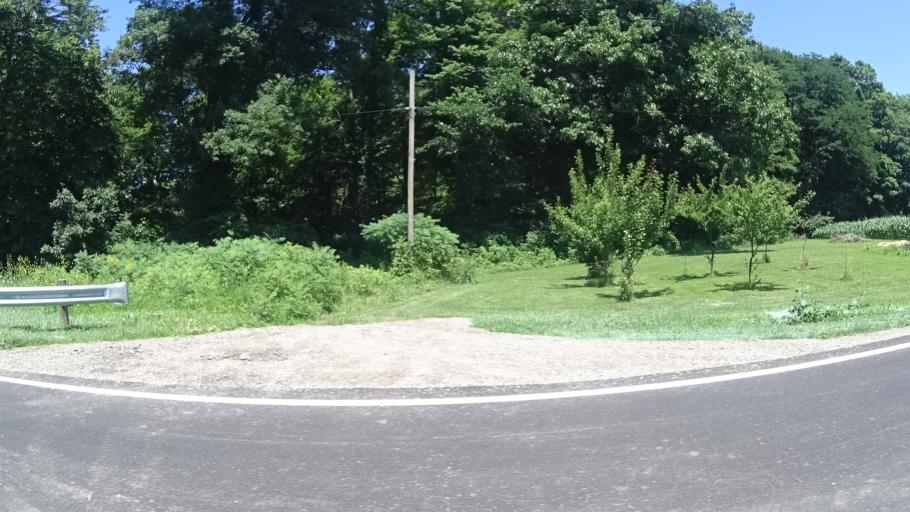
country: US
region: Ohio
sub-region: Huron County
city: Wakeman
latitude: 41.3463
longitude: -82.4403
